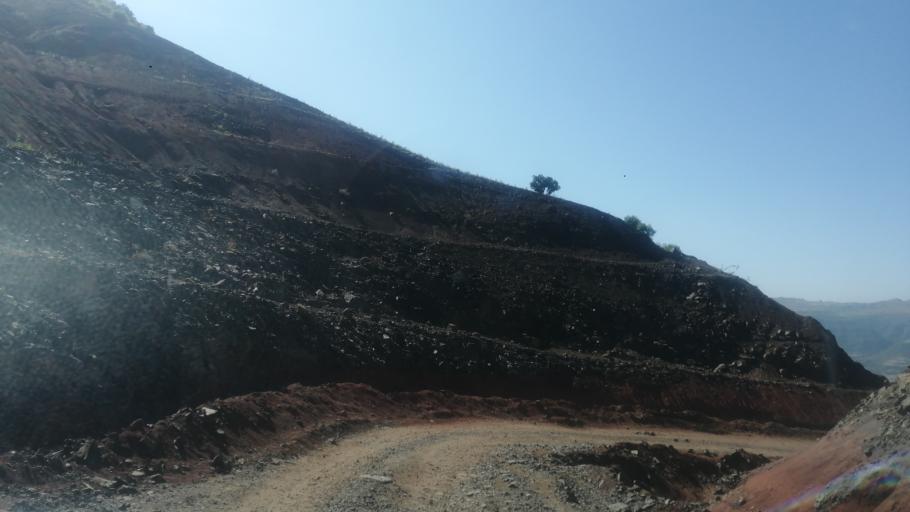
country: ET
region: Amhara
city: Addiet Canna
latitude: 11.1527
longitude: 37.8523
